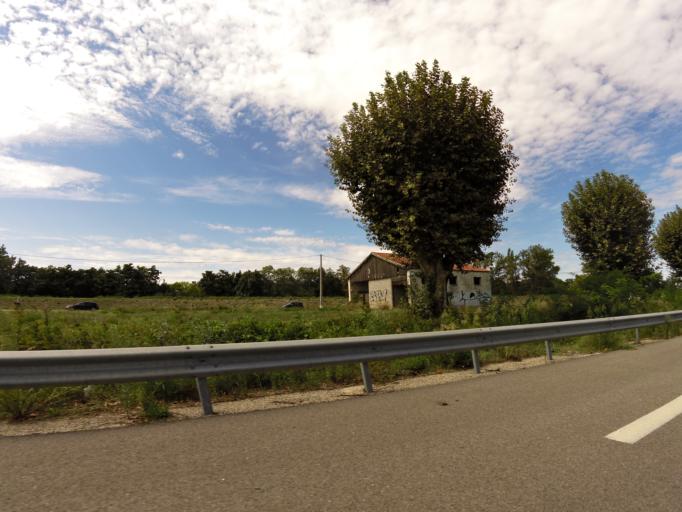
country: FR
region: Languedoc-Roussillon
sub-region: Departement de l'Herault
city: Marsillargues
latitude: 43.6397
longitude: 4.1936
